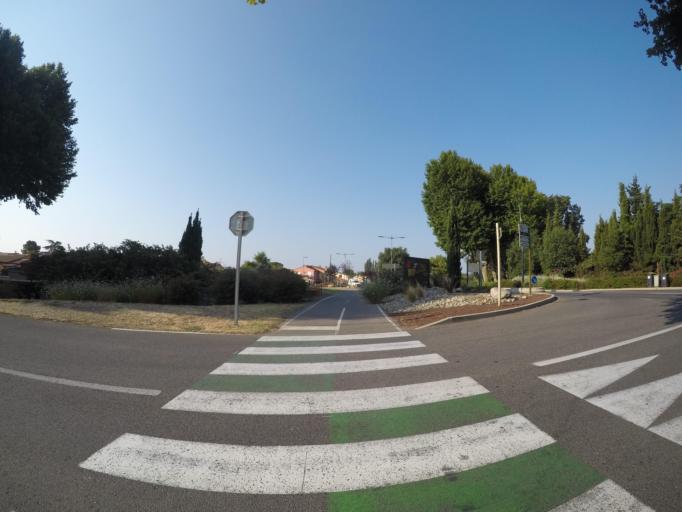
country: FR
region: Languedoc-Roussillon
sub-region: Departement des Pyrenees-Orientales
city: Canohes
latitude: 42.6583
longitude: 2.8348
